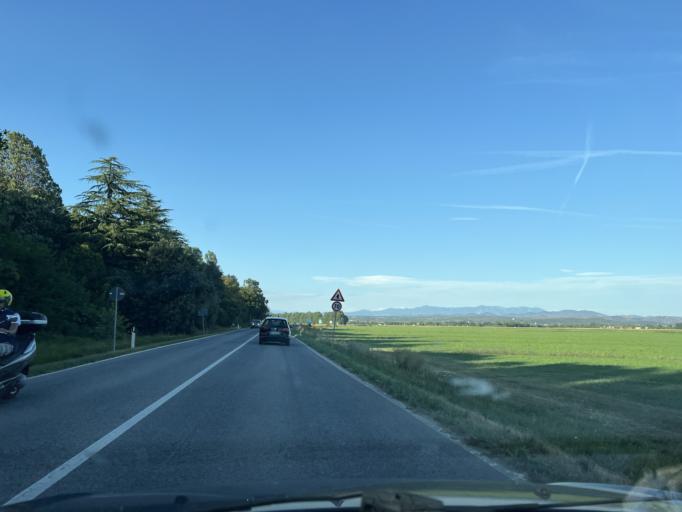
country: IT
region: Friuli Venezia Giulia
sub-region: Provincia di Gorizia
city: San Canzian d'Isonzo
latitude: 45.7868
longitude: 13.4769
